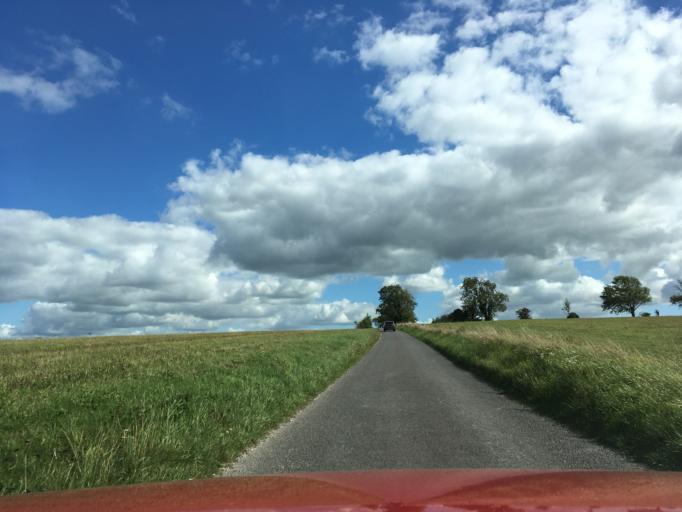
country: GB
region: England
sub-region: Wiltshire
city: Erlestoke
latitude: 51.2749
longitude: -2.0700
